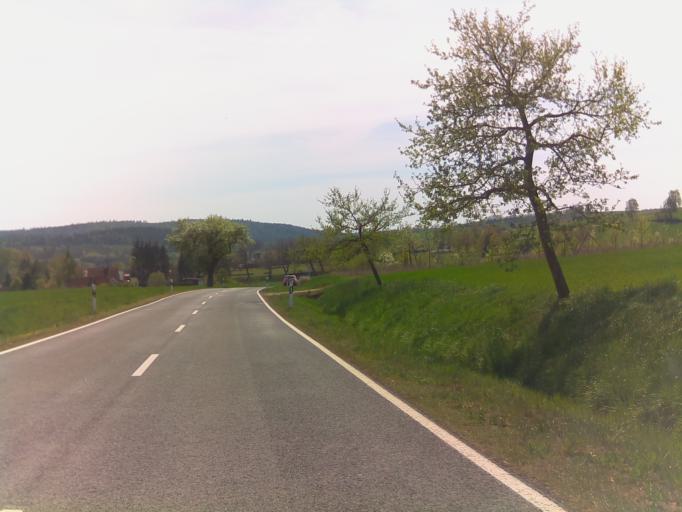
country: DE
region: Bavaria
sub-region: Regierungsbezirk Unterfranken
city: Ermershausen
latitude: 50.2145
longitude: 10.6220
